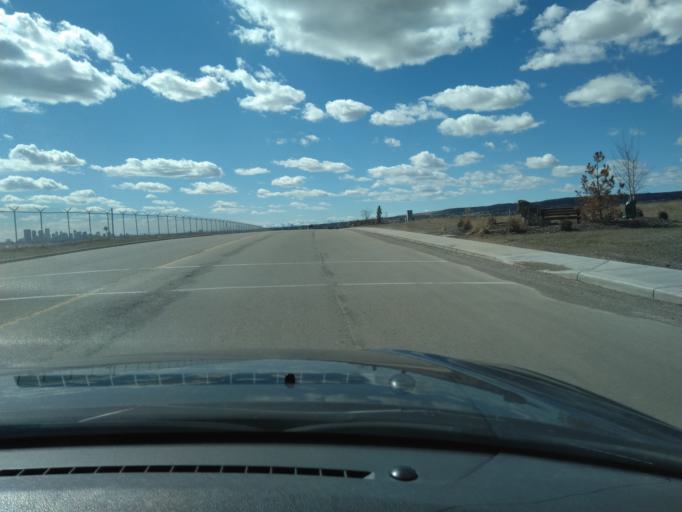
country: CA
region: Alberta
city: Calgary
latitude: 51.1308
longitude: -114.0386
